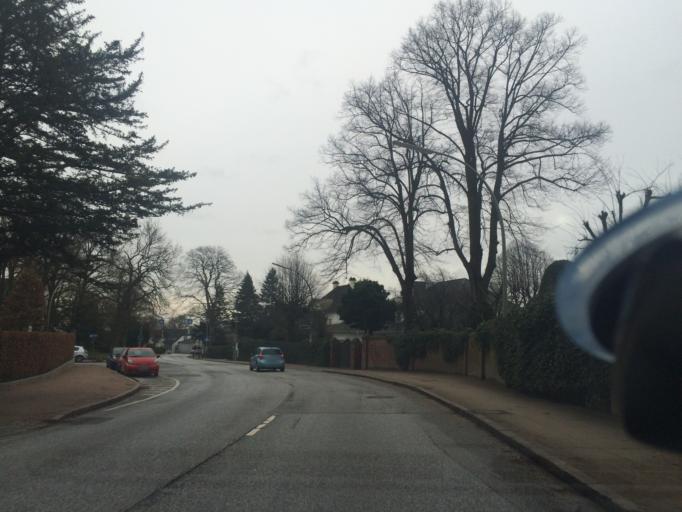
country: DE
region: Schleswig-Holstein
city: Halstenbek
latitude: 53.5517
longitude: 9.8410
